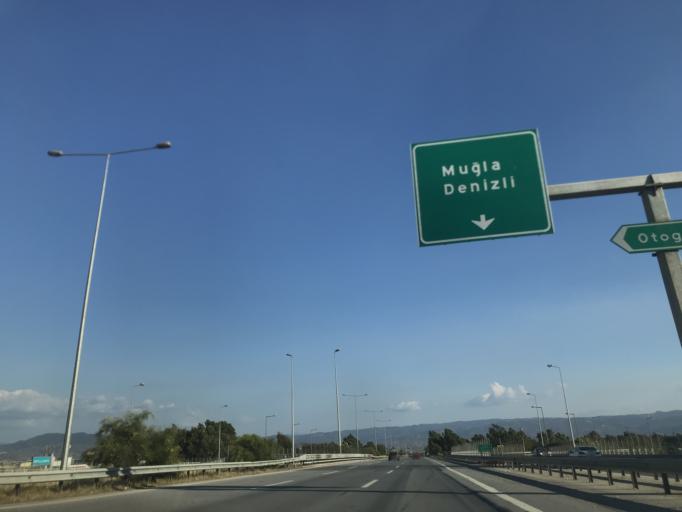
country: TR
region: Aydin
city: Aydin
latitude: 37.8485
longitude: 27.8072
